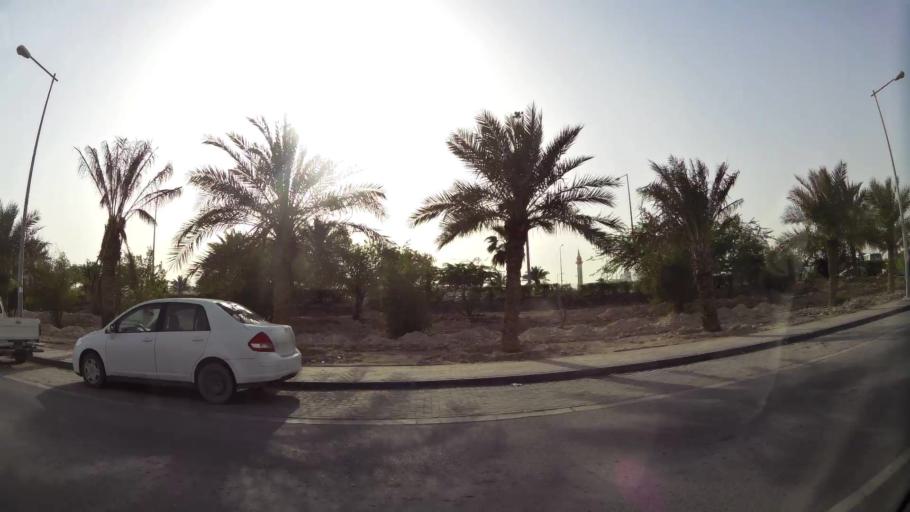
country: QA
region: Baladiyat ar Rayyan
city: Ar Rayyan
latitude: 25.2322
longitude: 51.4319
